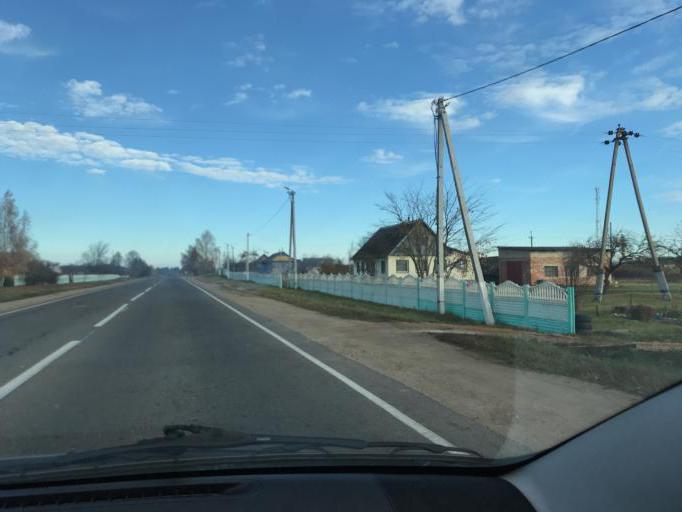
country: BY
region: Vitebsk
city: Haradok
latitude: 55.4844
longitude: 29.9680
